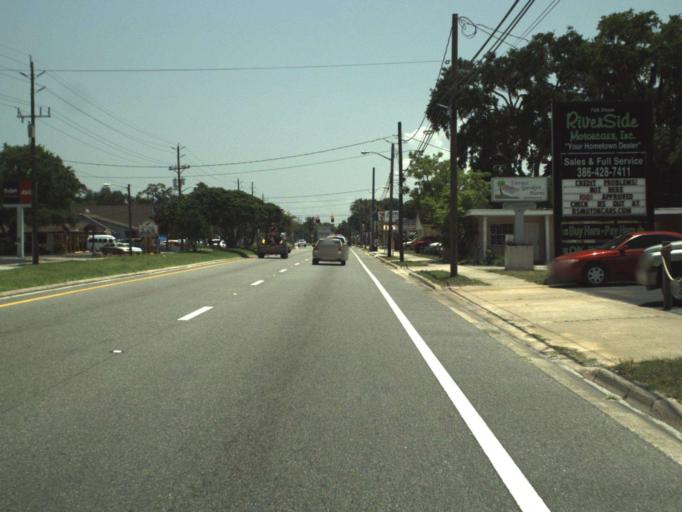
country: US
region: Florida
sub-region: Volusia County
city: New Smyrna Beach
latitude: 29.0360
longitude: -80.9317
